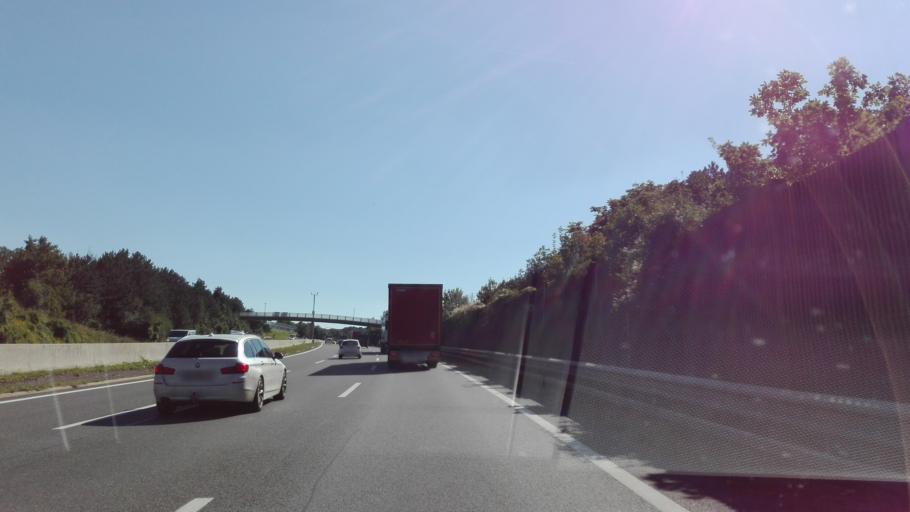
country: AT
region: Lower Austria
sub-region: Politischer Bezirk Modling
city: Perchtoldsdorf
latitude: 48.1077
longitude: 16.2598
